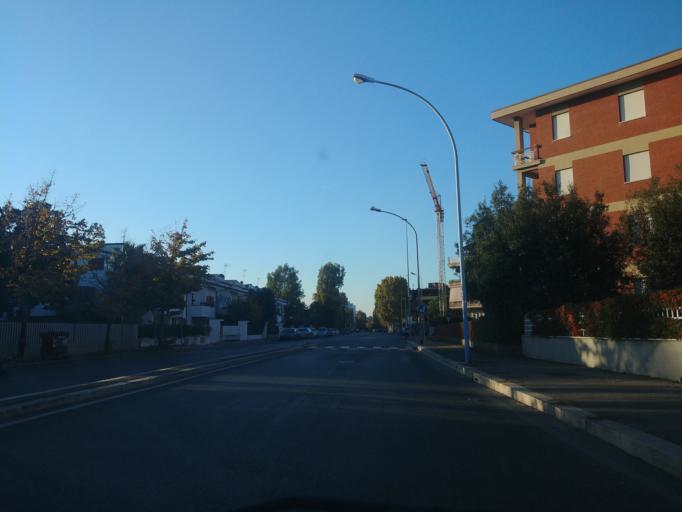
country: IT
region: Latium
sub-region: Provincia di Latina
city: Latina
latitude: 41.4580
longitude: 12.9025
